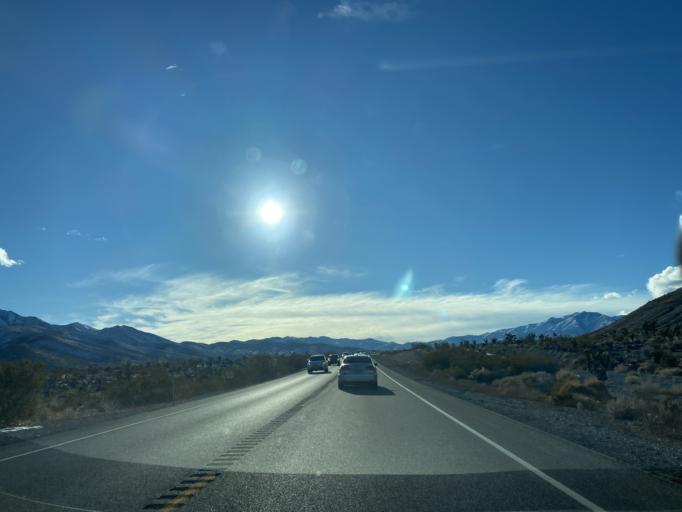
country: US
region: Nevada
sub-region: Clark County
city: Summerlin South
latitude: 36.2850
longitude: -115.4364
